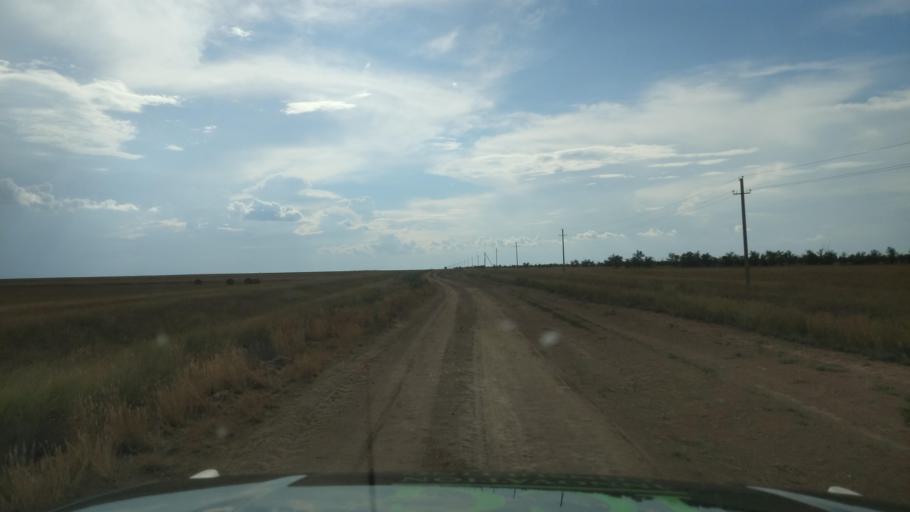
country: KZ
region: Pavlodar
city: Pavlodar
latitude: 52.5125
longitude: 77.5054
